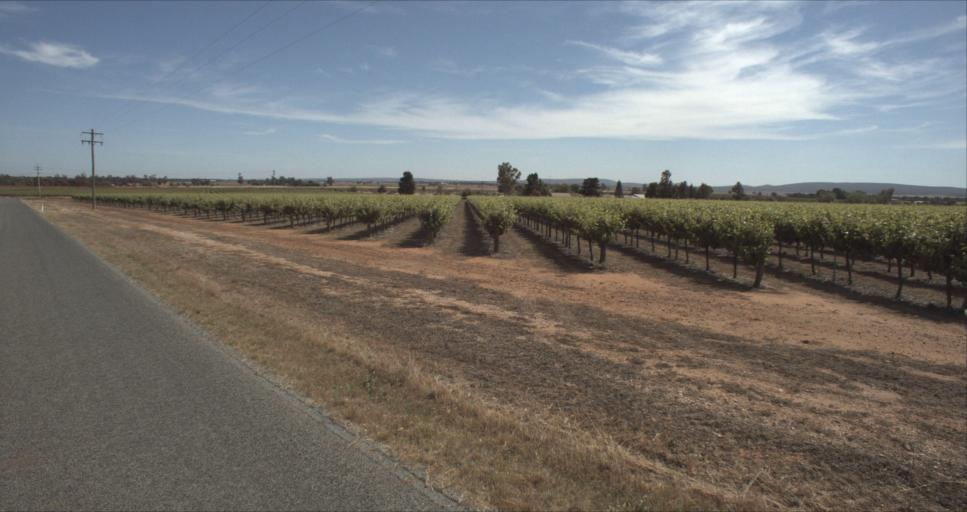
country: AU
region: New South Wales
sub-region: Leeton
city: Leeton
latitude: -34.5699
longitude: 146.4454
